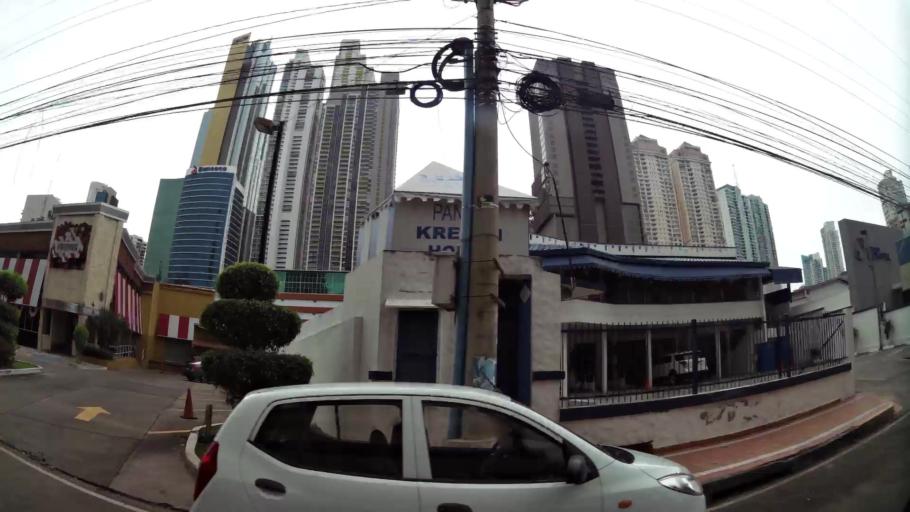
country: PA
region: Panama
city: Panama
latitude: 8.9786
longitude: -79.5244
